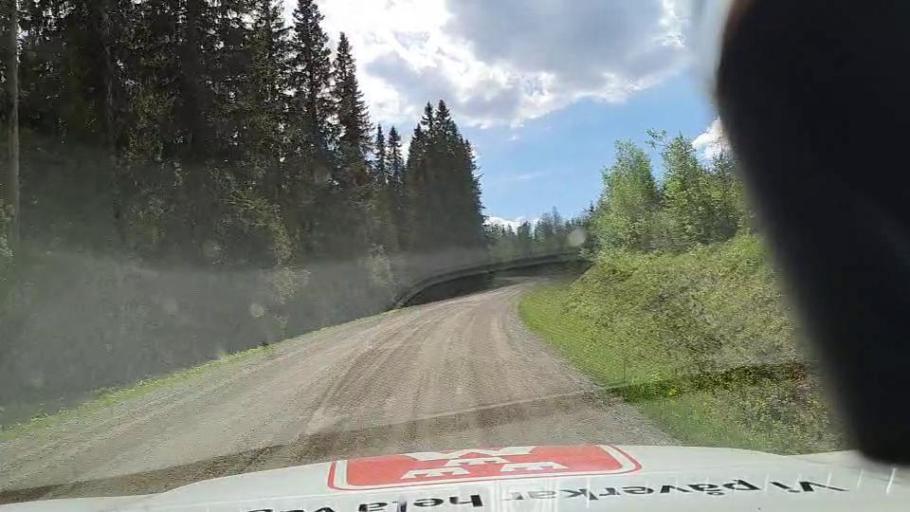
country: SE
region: Vaesterbotten
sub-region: Vilhelmina Kommun
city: Sjoberg
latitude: 64.5620
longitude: 15.8477
